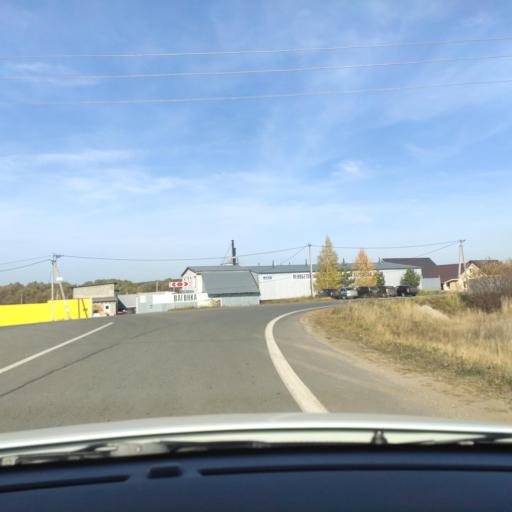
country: RU
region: Tatarstan
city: Vysokaya Gora
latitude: 55.7470
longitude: 49.4006
